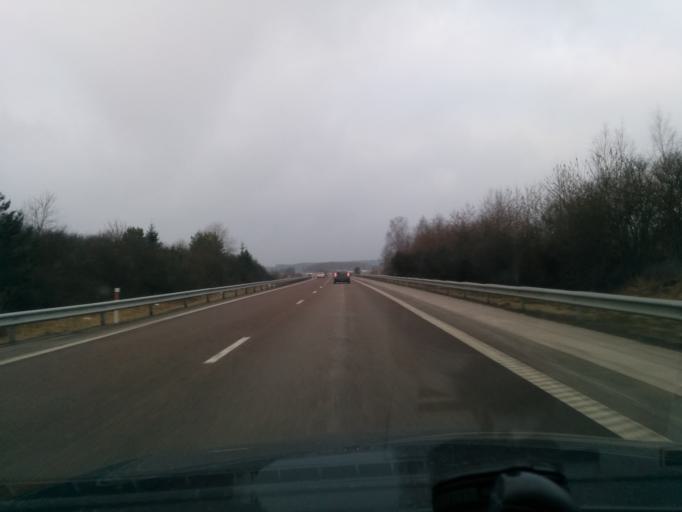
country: SE
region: Uppsala
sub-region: Enkopings Kommun
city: Grillby
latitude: 59.6390
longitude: 17.2593
